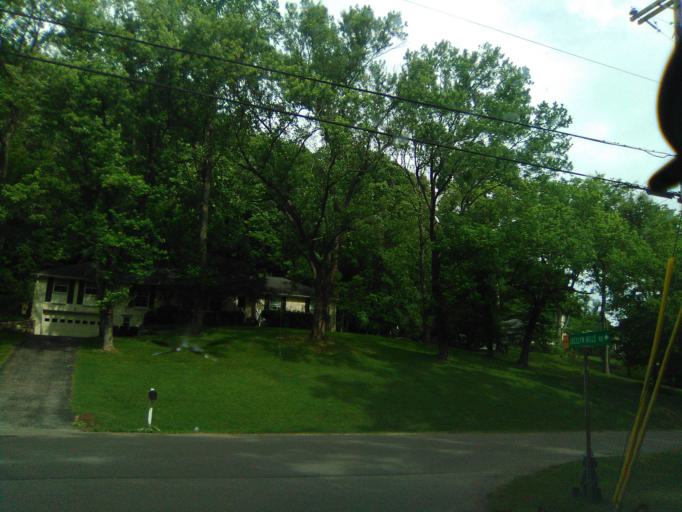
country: US
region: Tennessee
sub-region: Davidson County
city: Belle Meade
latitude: 36.0986
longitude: -86.9022
